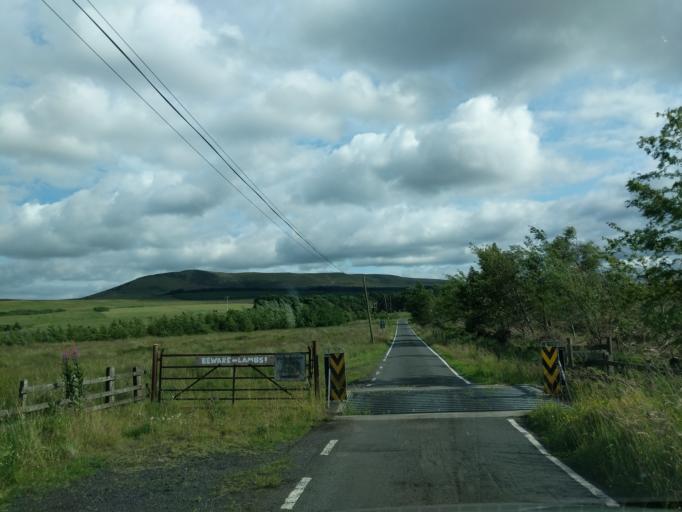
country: GB
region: Scotland
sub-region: West Lothian
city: East Calder
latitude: 55.8334
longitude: -3.4574
